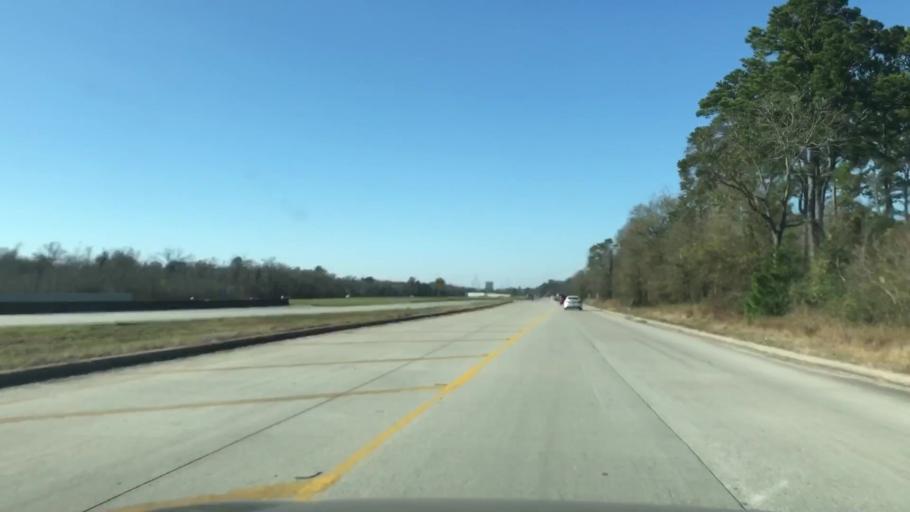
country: US
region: Texas
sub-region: Harris County
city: Cloverleaf
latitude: 29.8276
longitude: -95.1884
